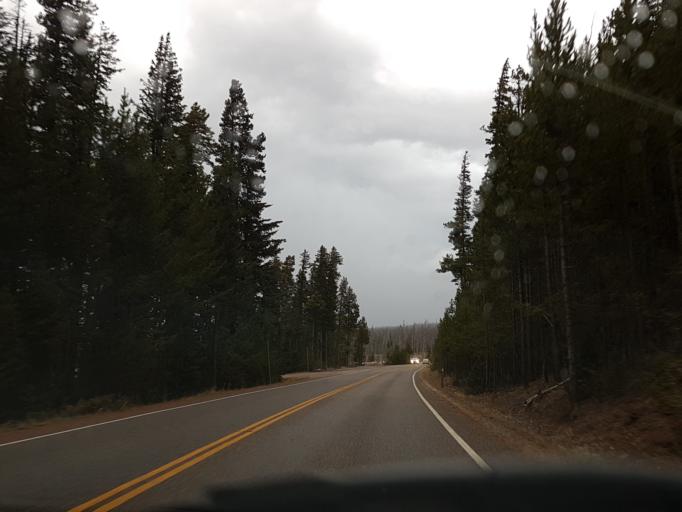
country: US
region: Montana
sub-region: Gallatin County
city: West Yellowstone
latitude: 44.4656
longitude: -110.5162
